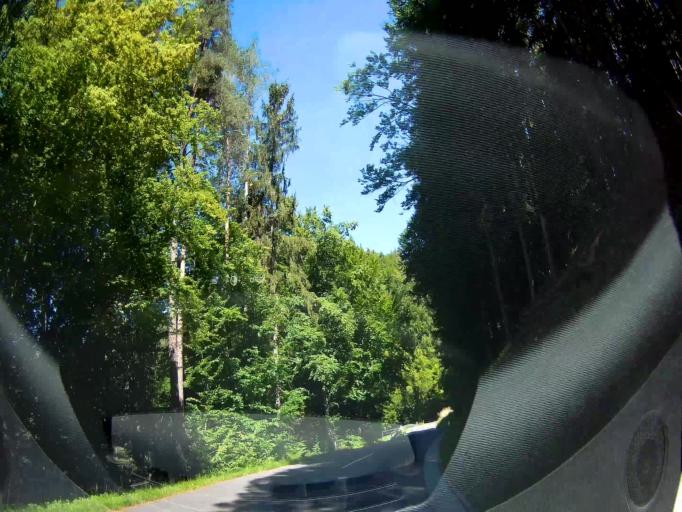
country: AT
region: Carinthia
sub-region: Politischer Bezirk Klagenfurt Land
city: Maria Worth
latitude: 46.5932
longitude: 14.1585
